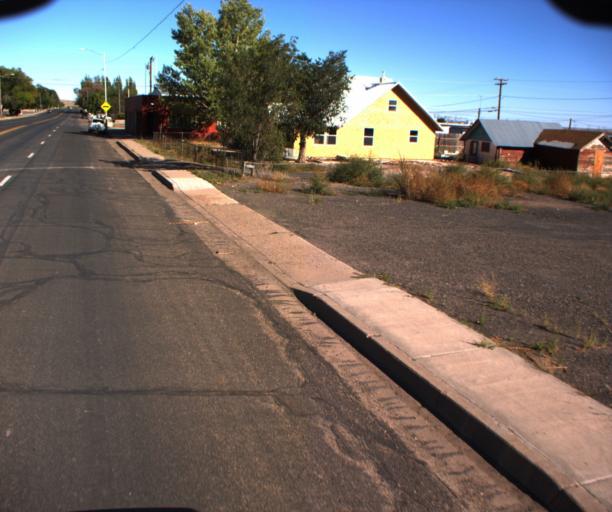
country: US
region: Arizona
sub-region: Navajo County
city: Joseph City
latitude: 34.9560
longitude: -110.3356
